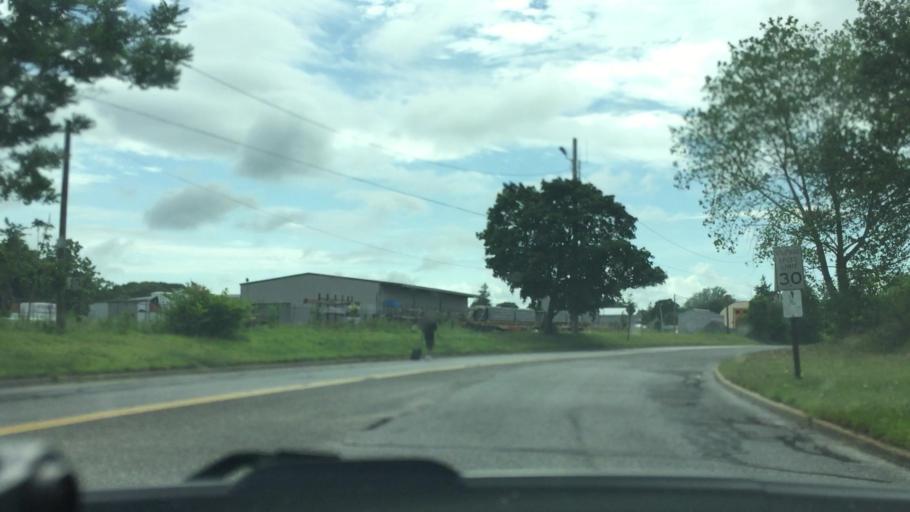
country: US
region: New York
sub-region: Suffolk County
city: Port Jefferson Station
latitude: 40.9338
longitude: -73.0461
